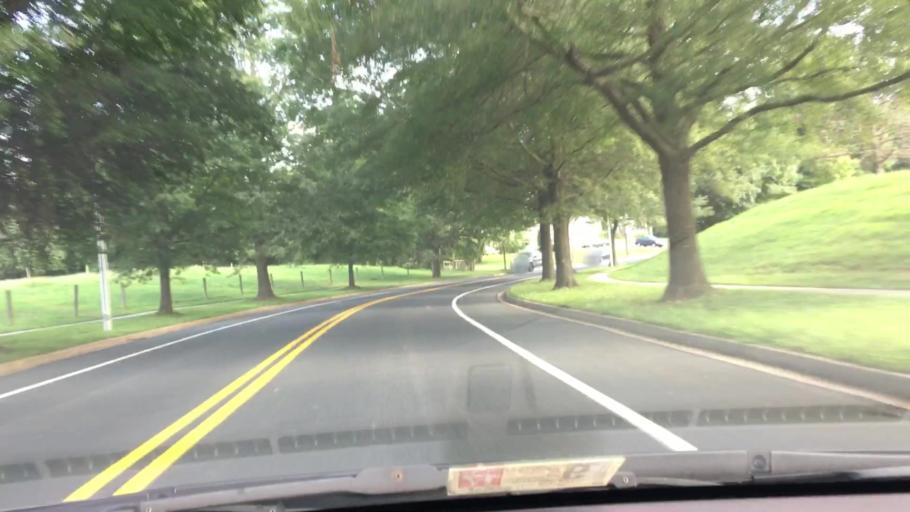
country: US
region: Maryland
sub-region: Montgomery County
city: Olney
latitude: 39.1572
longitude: -77.0488
